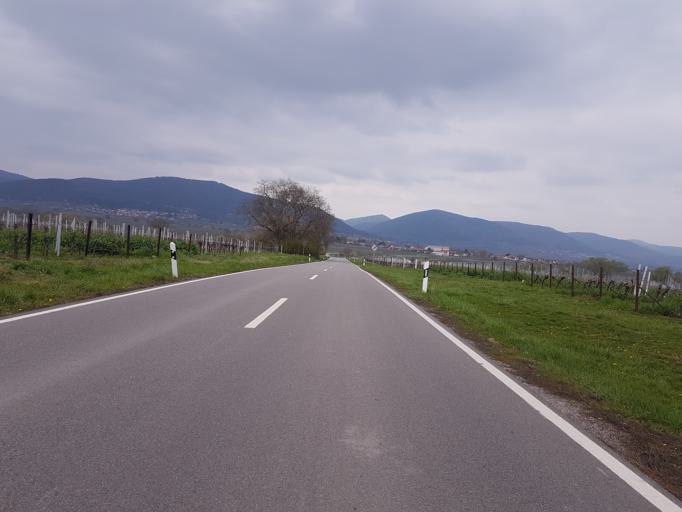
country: DE
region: Rheinland-Pfalz
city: Bochingen
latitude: 49.2261
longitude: 8.1000
